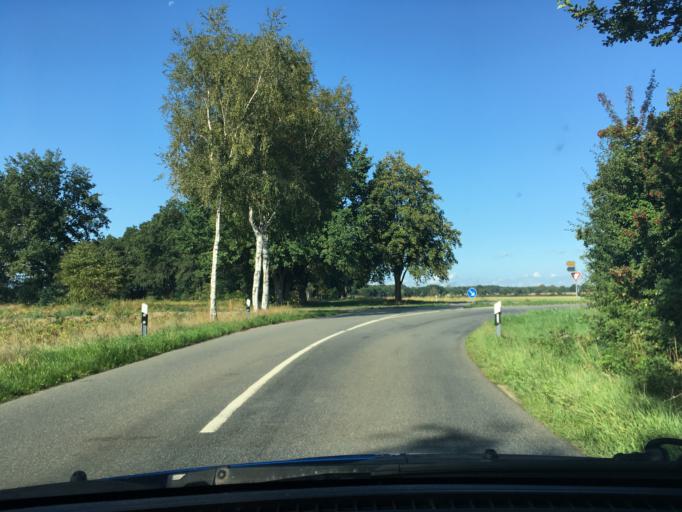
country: DE
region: Lower Saxony
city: Wriedel
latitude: 53.0074
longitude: 10.2790
